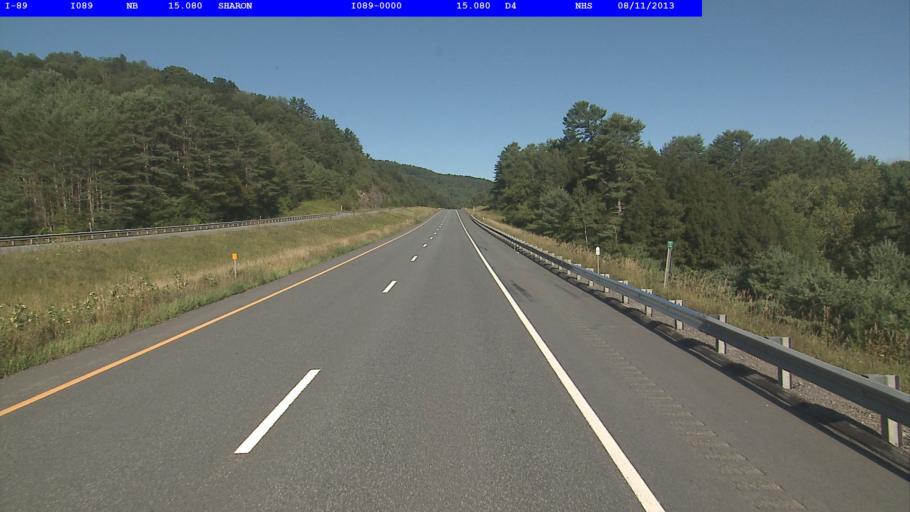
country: US
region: Vermont
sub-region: Windsor County
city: Woodstock
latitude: 43.7833
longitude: -72.4843
